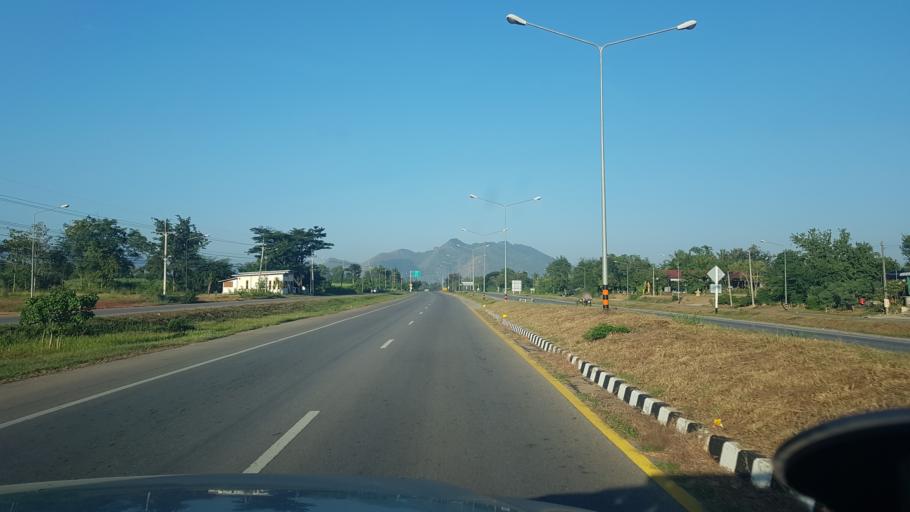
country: TH
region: Chaiyaphum
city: Khon San
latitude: 16.5955
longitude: 101.9241
